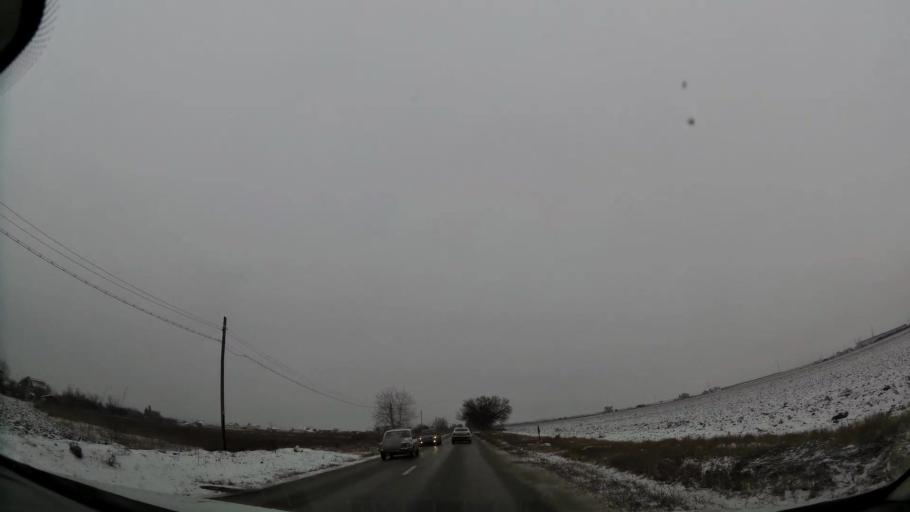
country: RO
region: Dambovita
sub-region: Comuna Ulmi
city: Ulmi
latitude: 44.8916
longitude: 25.5168
